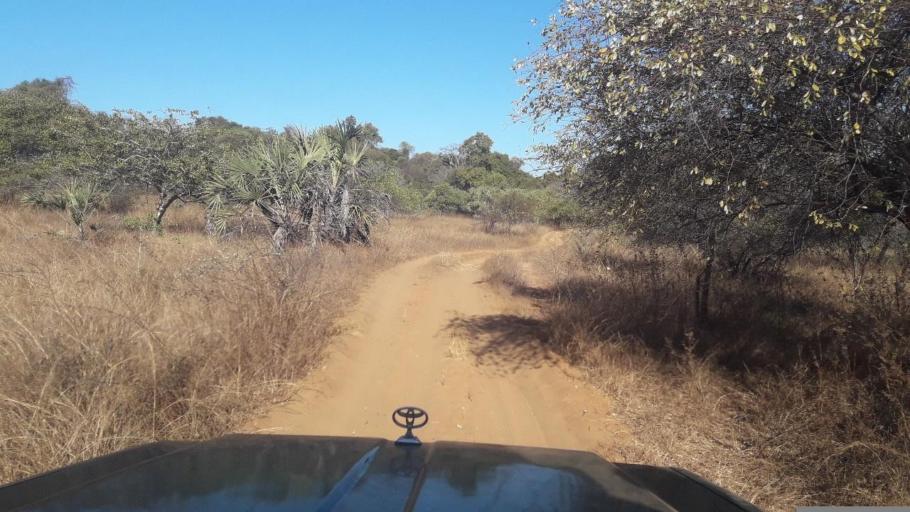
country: MG
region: Boeny
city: Sitampiky
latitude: -16.4131
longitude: 45.6048
